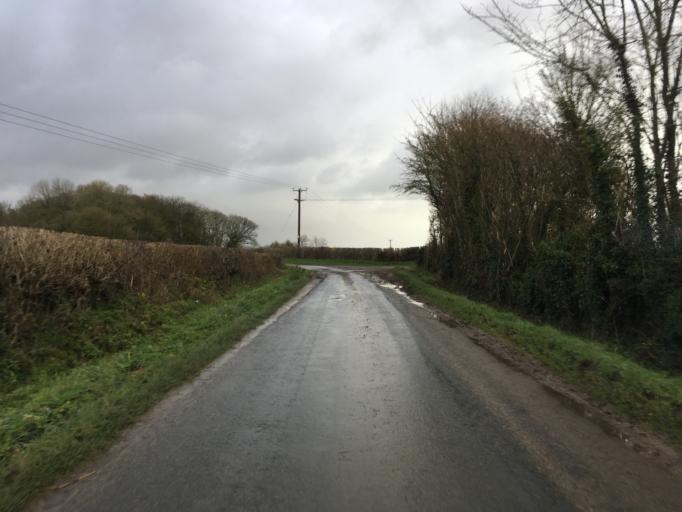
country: GB
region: England
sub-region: Wiltshire
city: Malmesbury
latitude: 51.6331
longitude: -2.1061
